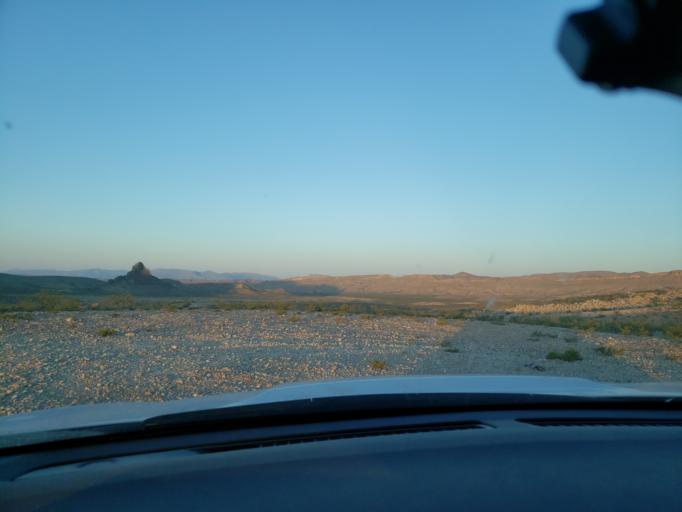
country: US
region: Texas
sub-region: Culberson County
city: Van Horn
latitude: 30.7186
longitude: -104.7696
